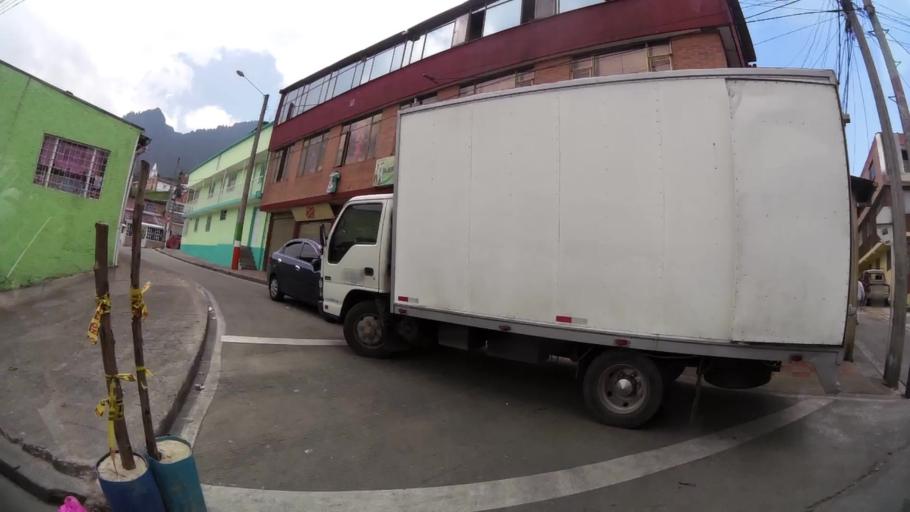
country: CO
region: Bogota D.C.
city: Bogota
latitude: 4.5852
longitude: -74.0676
